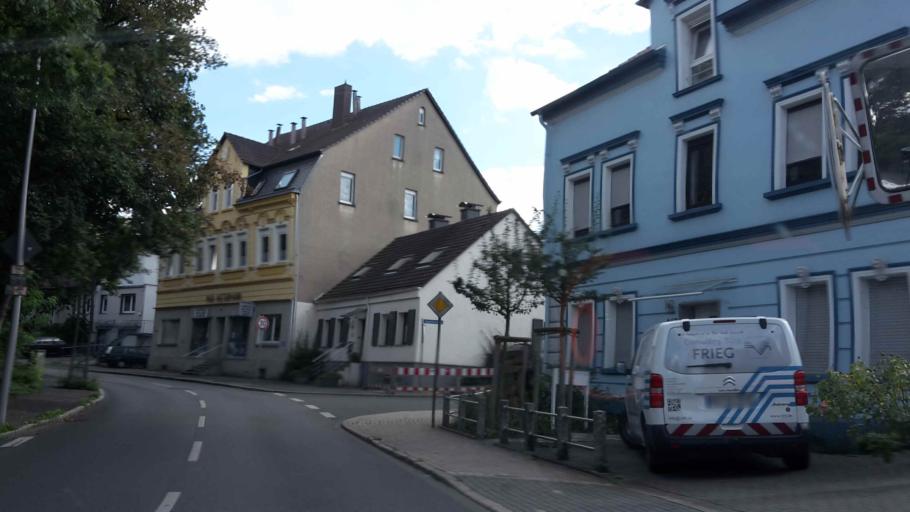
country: DE
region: North Rhine-Westphalia
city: Hattingen
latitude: 51.4364
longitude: 7.1579
